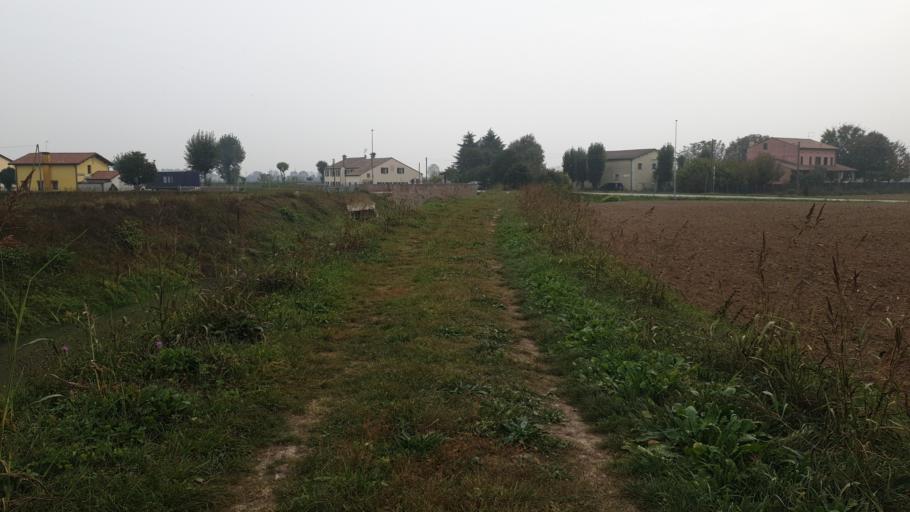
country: IT
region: Veneto
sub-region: Provincia di Padova
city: Casalserugo
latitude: 45.3316
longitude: 11.9280
